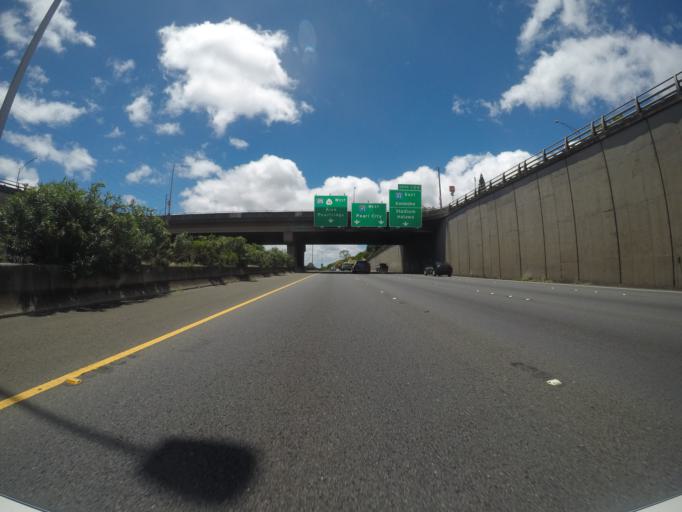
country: US
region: Hawaii
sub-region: Honolulu County
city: Halawa Heights
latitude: 21.3661
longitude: -157.9036
